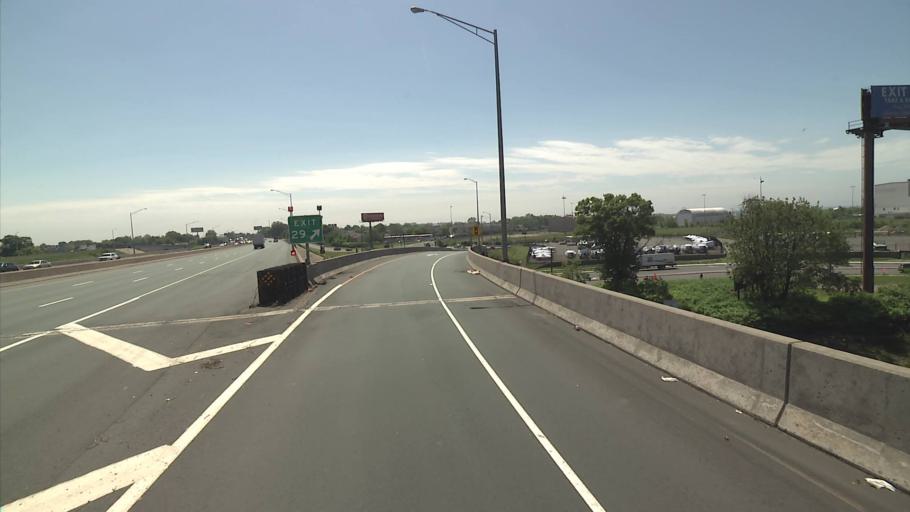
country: US
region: Connecticut
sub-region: Fairfield County
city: Bridgeport
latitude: 41.1777
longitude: -73.1750
